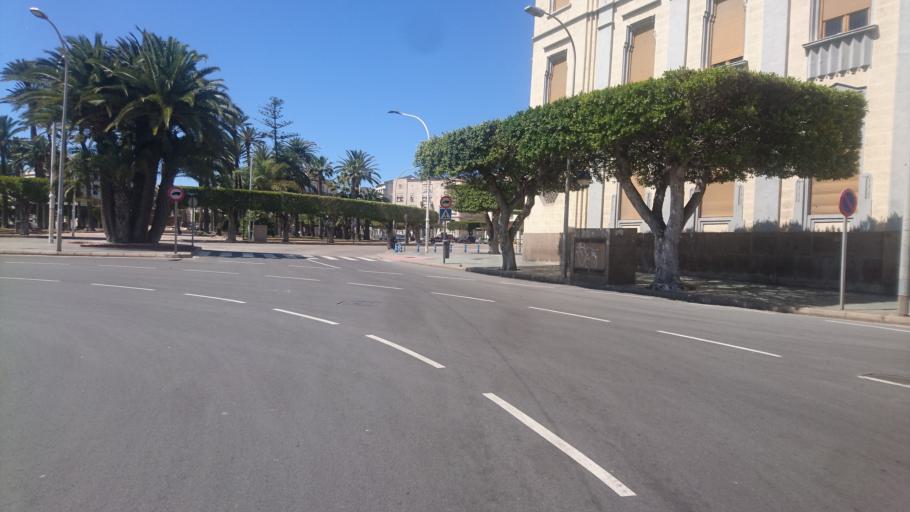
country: ES
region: Melilla
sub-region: Melilla
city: Melilla
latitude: 35.2916
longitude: -2.9369
